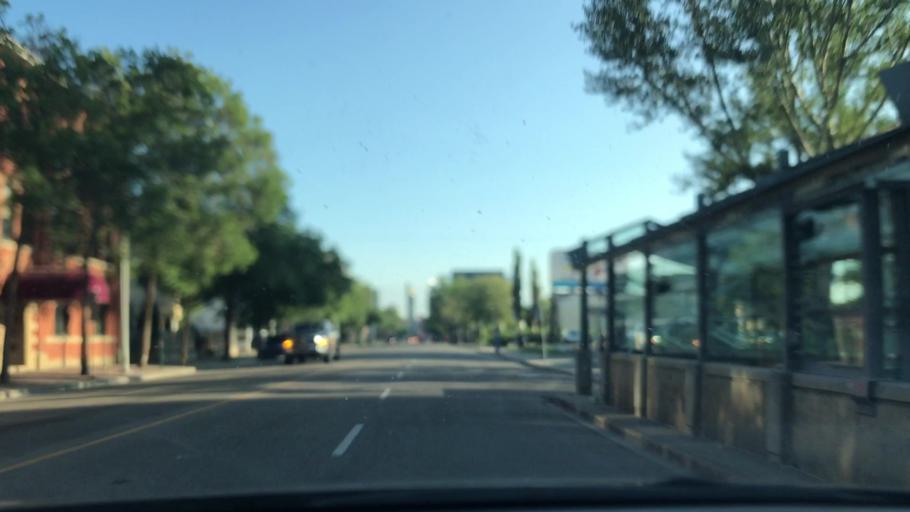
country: CA
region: Alberta
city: Edmonton
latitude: 53.5410
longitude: -113.5048
